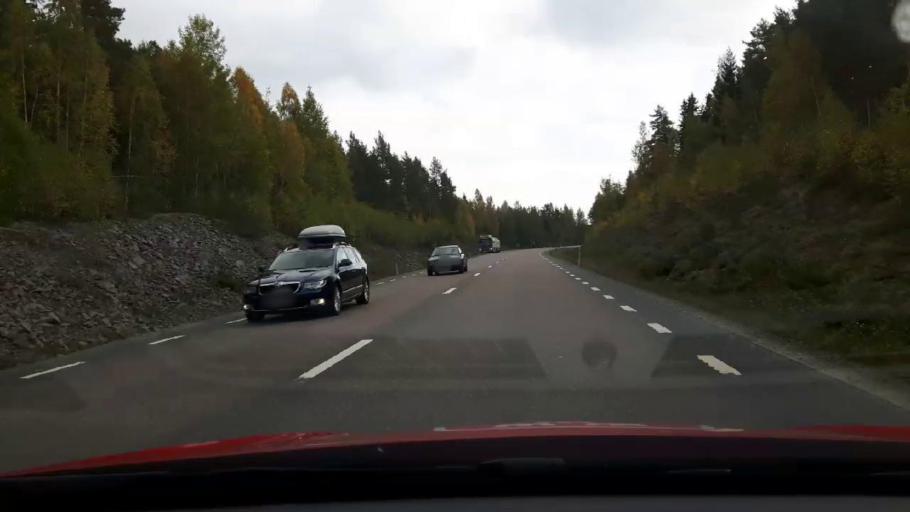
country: SE
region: Gaevleborg
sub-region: Bollnas Kommun
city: Kilafors
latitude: 61.2717
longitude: 16.5352
